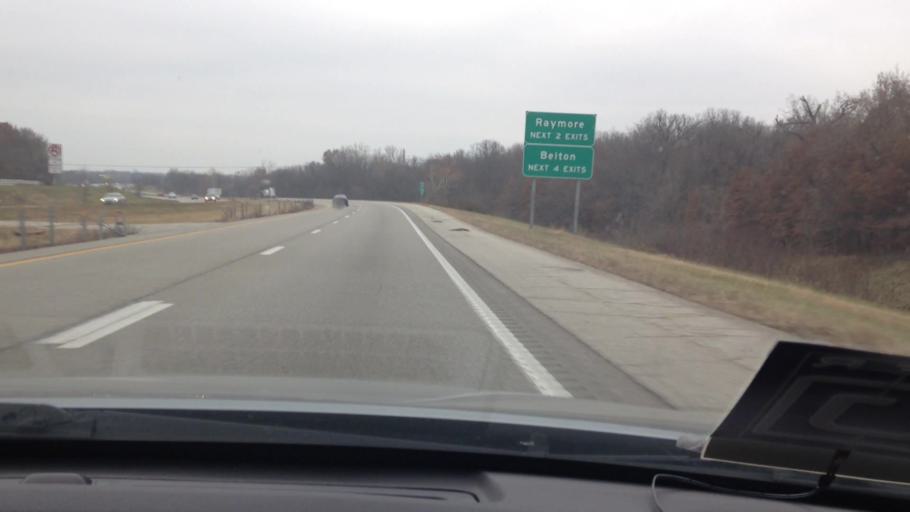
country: US
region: Missouri
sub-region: Cass County
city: Peculiar
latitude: 38.7553
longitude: -94.4815
